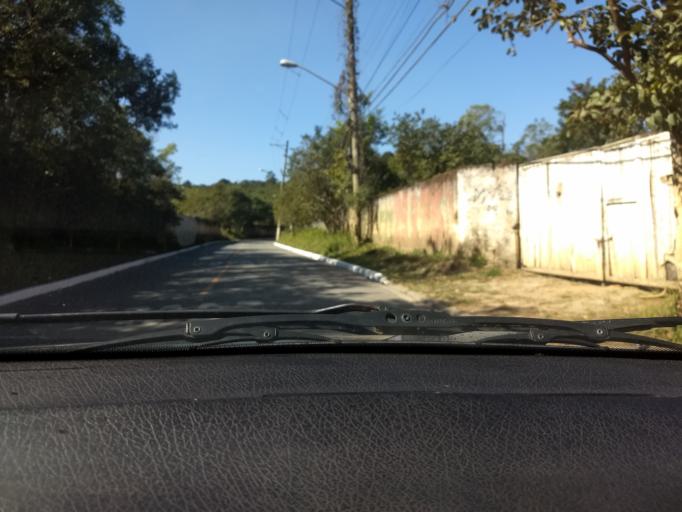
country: BR
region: Sao Paulo
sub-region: Embu-Guacu
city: Embu Guacu
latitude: -23.8110
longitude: -46.7561
